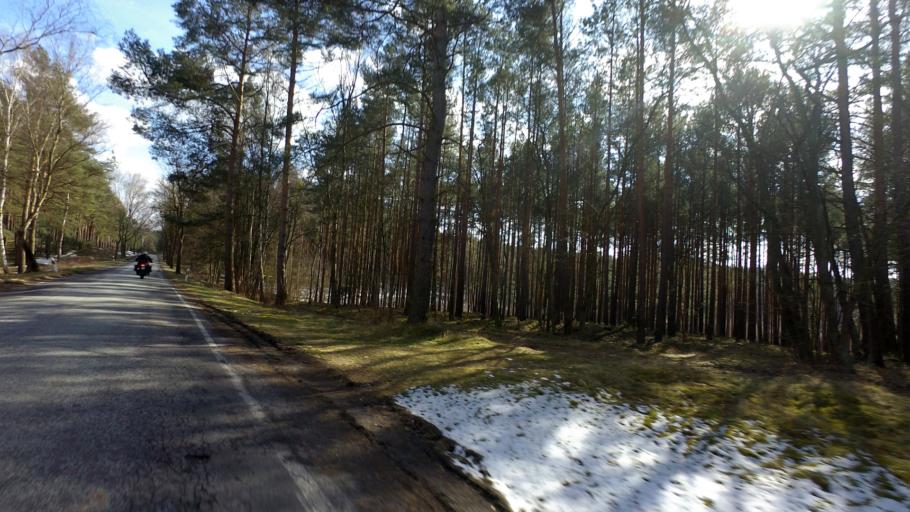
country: DE
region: Brandenburg
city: Biesenthal
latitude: 52.7826
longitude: 13.6111
